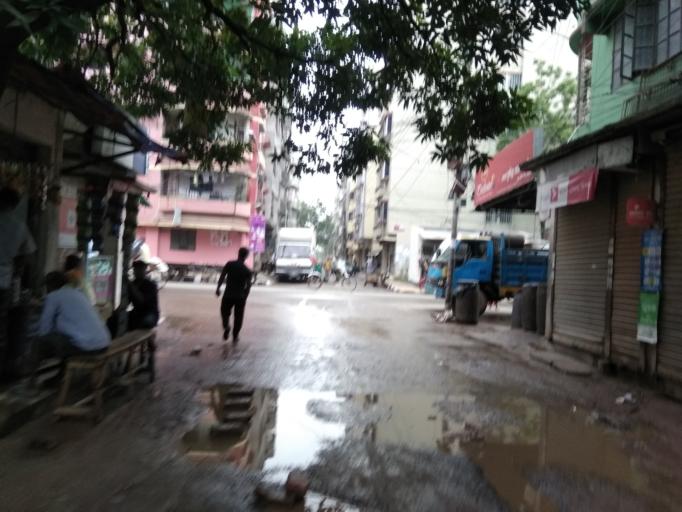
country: BD
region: Dhaka
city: Tungi
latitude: 23.8259
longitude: 90.3734
